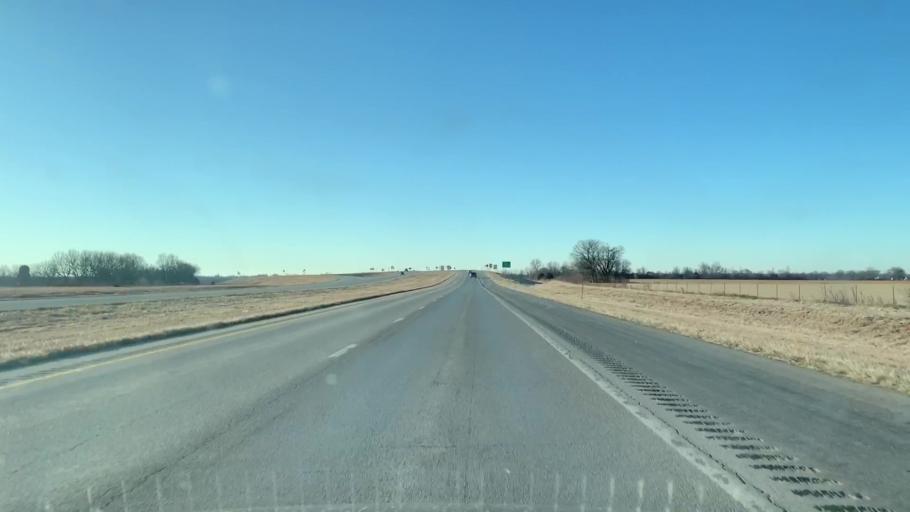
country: US
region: Kansas
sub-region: Bourbon County
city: Fort Scott
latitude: 37.7753
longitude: -94.7058
